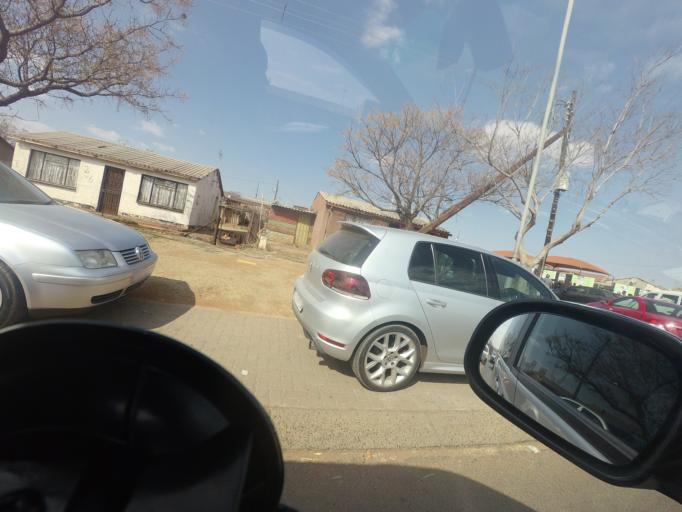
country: ZA
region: Gauteng
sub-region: Sedibeng District Municipality
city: Heidelberg
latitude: -26.5506
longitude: 28.3302
